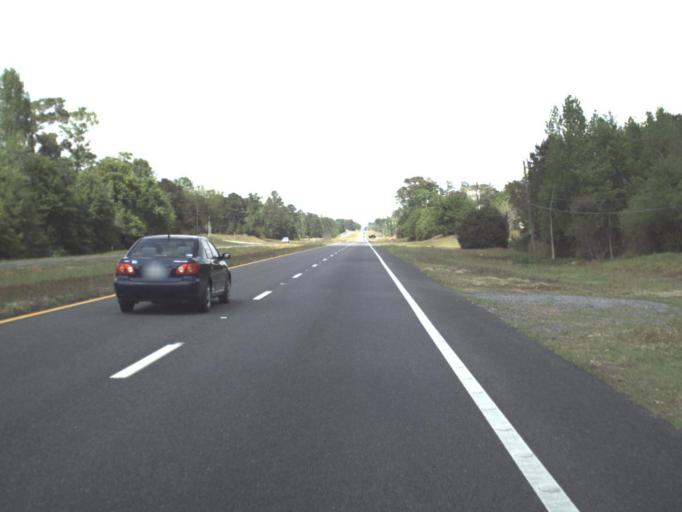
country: US
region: Florida
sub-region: Escambia County
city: Century
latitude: 30.9416
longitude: -87.2906
